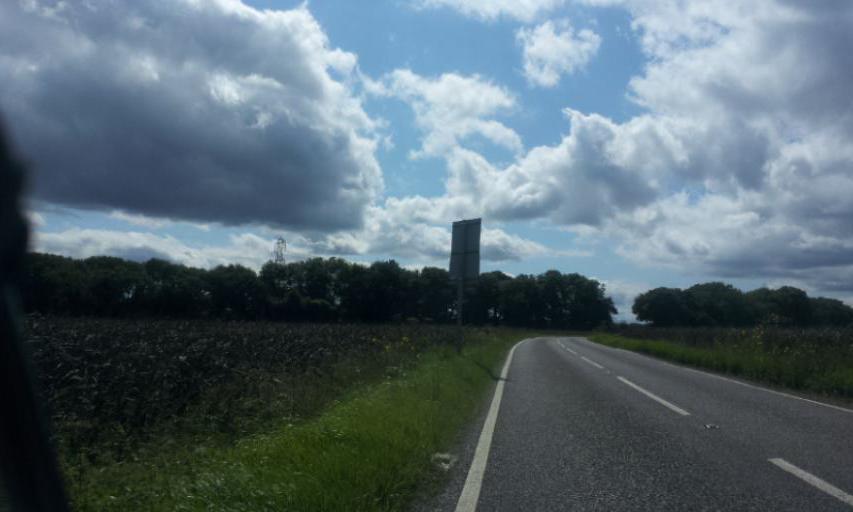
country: GB
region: England
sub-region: Kent
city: Boxley
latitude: 51.3236
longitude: 0.5601
